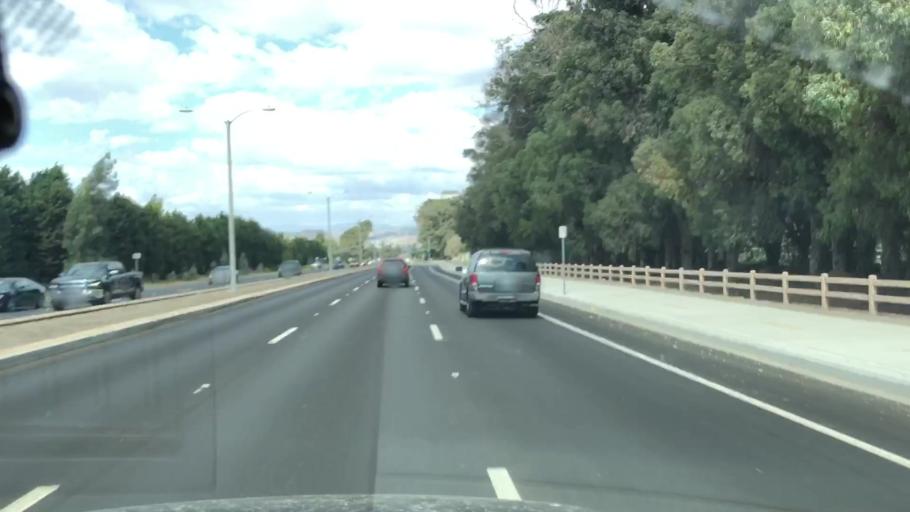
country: US
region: California
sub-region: Ventura County
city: Oxnard Shores
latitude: 34.2223
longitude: -119.2210
